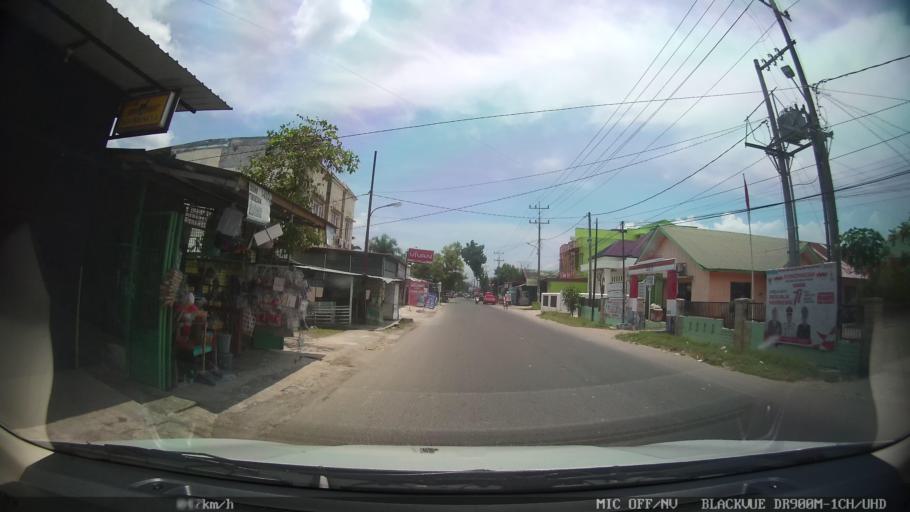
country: ID
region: North Sumatra
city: Binjai
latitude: 3.6112
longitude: 98.5179
